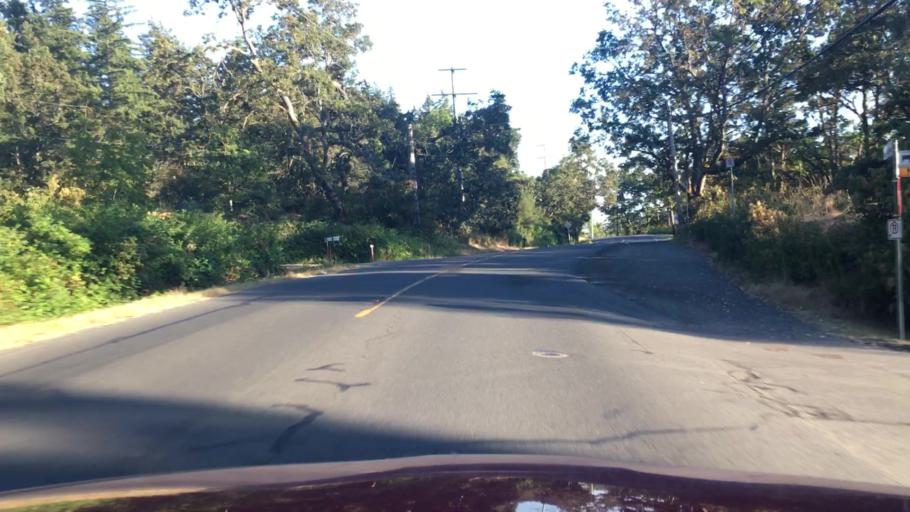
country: CA
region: British Columbia
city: Victoria
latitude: 48.4914
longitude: -123.3558
